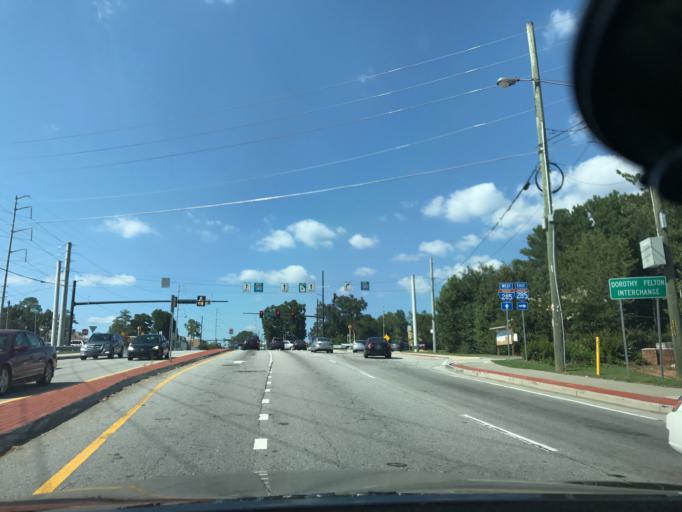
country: US
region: Georgia
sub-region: Fulton County
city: Sandy Springs
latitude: 33.9107
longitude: -84.3789
